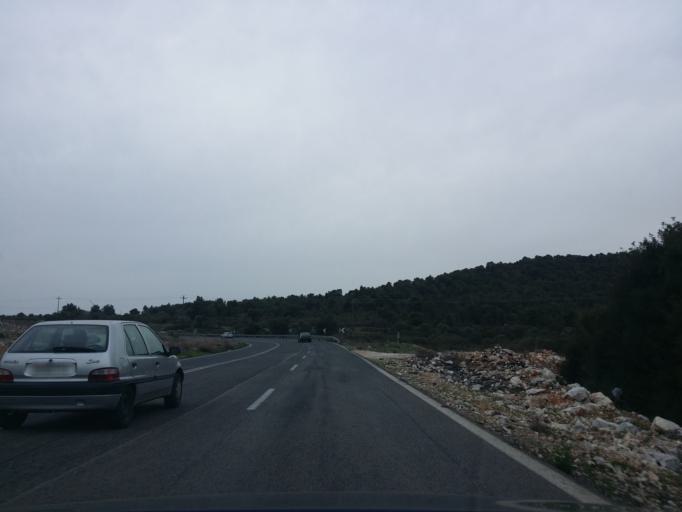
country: GR
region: Attica
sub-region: Nomarchia Dytikis Attikis
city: Vilia
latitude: 38.1598
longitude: 23.4295
